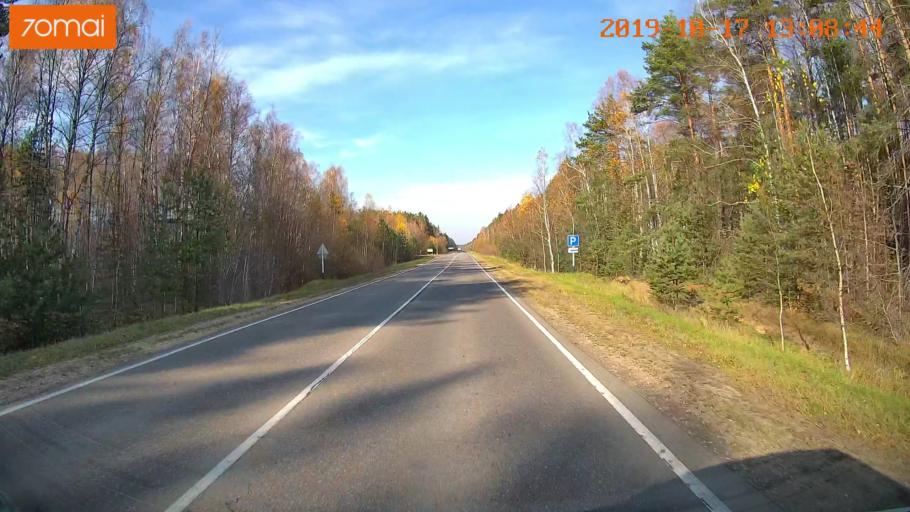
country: RU
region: Rjazan
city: Syntul
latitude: 54.9931
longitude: 41.2674
